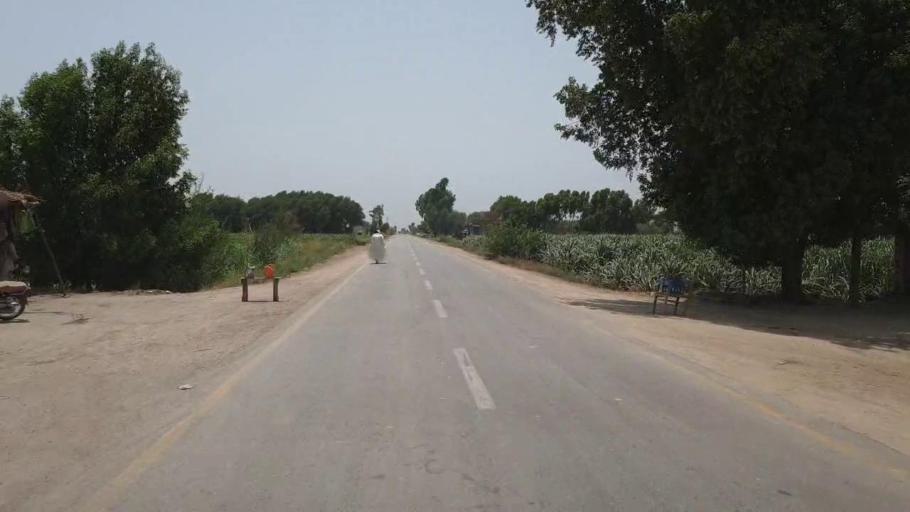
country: PK
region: Sindh
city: Moro
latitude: 26.5986
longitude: 68.1032
